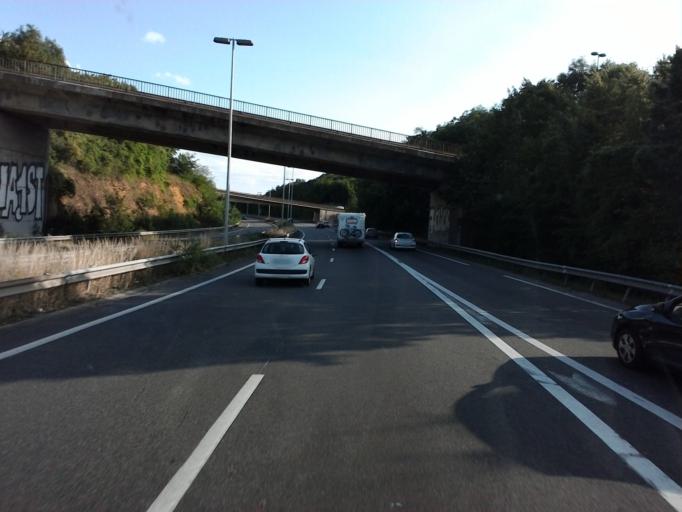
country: FR
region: Lorraine
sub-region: Departement de Meurthe-et-Moselle
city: Laxou
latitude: 48.6961
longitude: 6.1171
